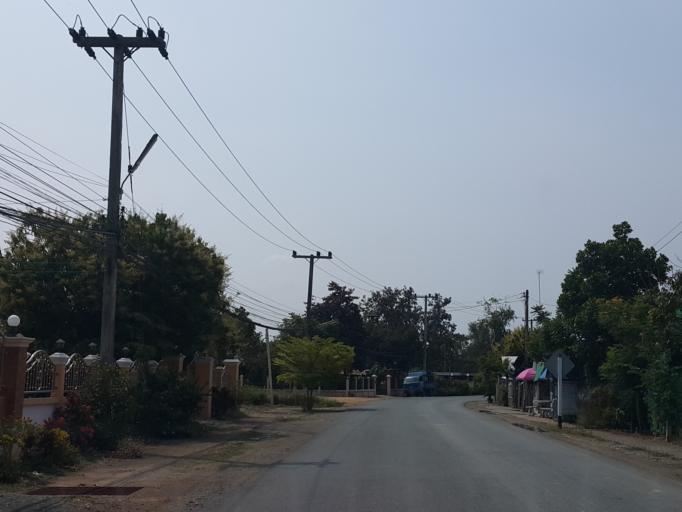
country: TH
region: Lamphun
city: Ban Thi
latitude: 18.6775
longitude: 99.1006
